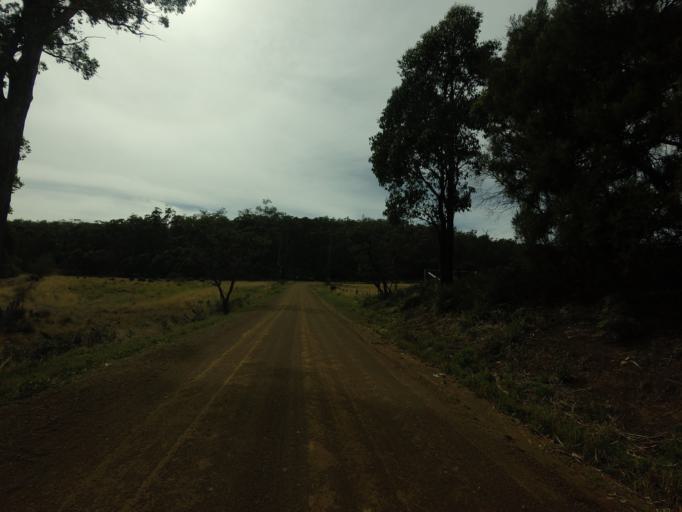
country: AU
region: Tasmania
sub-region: Sorell
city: Sorell
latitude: -42.4782
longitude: 147.6105
